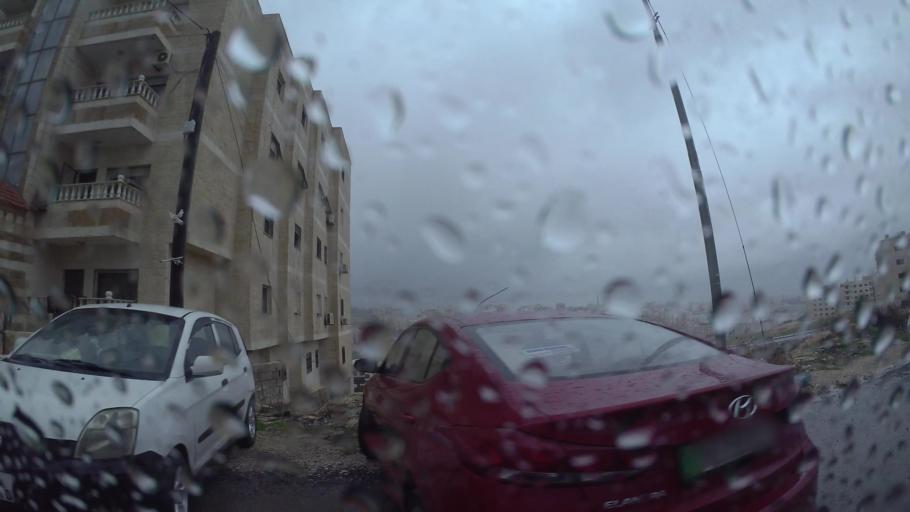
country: JO
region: Amman
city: Al Jubayhah
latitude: 32.0375
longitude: 35.8819
